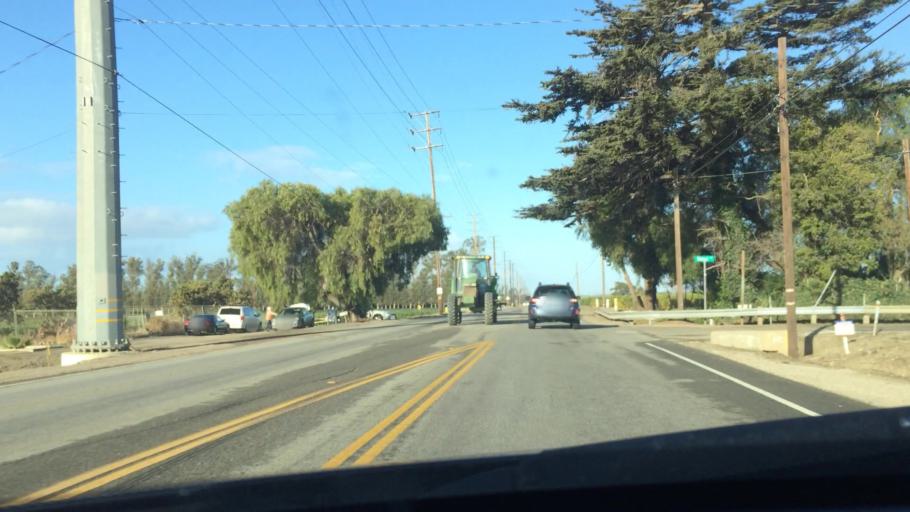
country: US
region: California
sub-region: Ventura County
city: Camarillo
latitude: 34.2637
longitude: -119.0764
